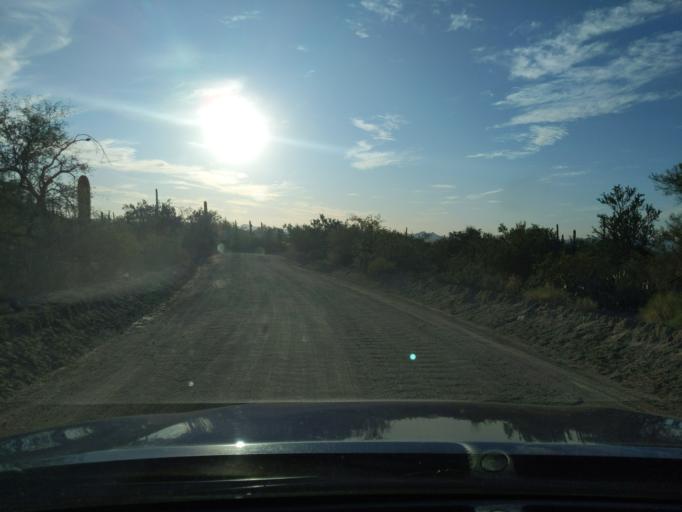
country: US
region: Arizona
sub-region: Pima County
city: Picture Rocks
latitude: 32.2883
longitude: -111.1906
